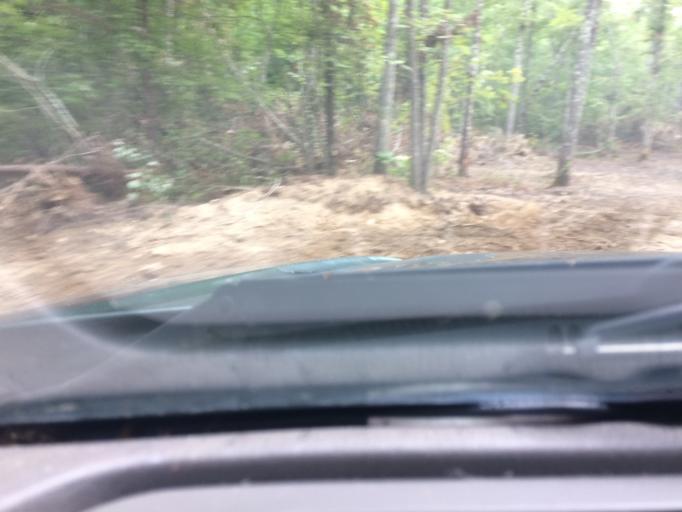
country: US
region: Tennessee
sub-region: Fentress County
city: Grimsley
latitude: 36.1939
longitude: -84.8787
